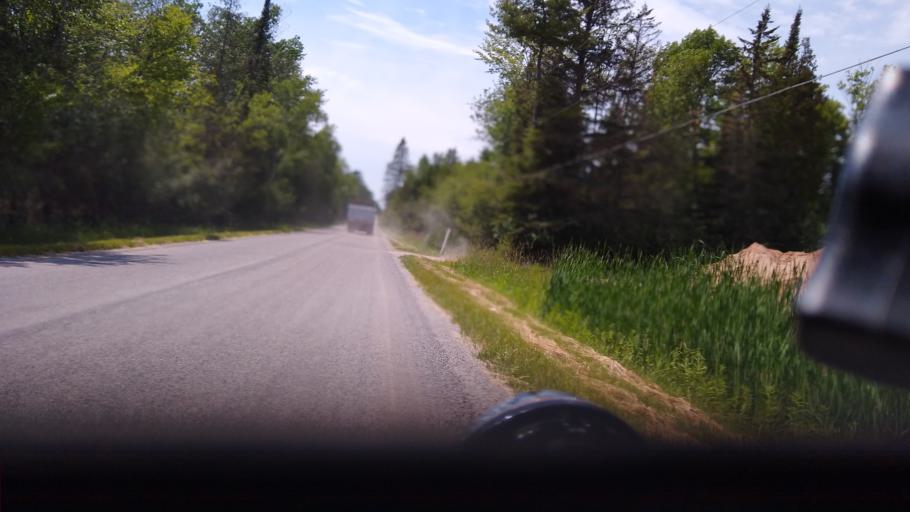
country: US
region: Michigan
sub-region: Delta County
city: Escanaba
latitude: 45.7102
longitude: -87.1437
